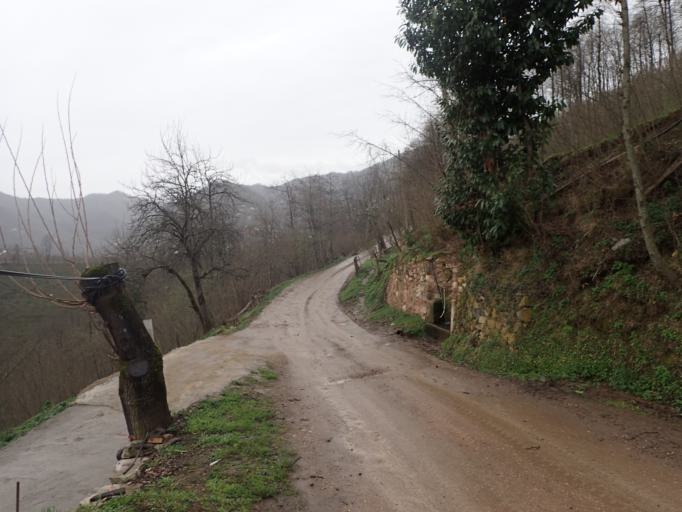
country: TR
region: Ordu
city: Camas
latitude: 40.8863
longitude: 37.5060
